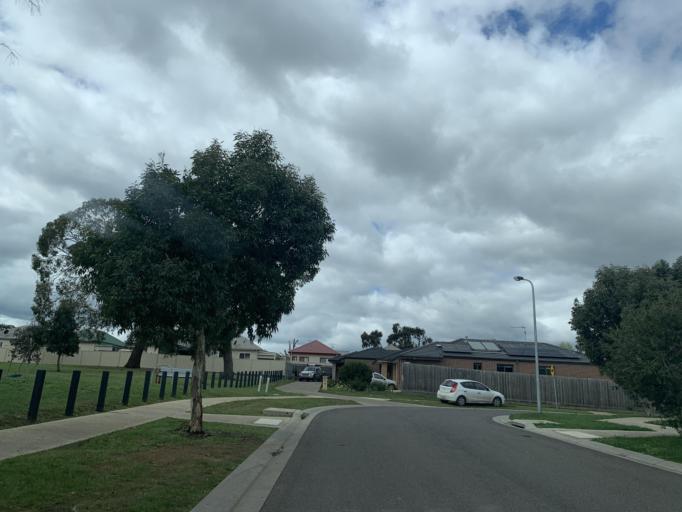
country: AU
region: Victoria
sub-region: Whittlesea
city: Whittlesea
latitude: -37.2917
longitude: 144.9310
